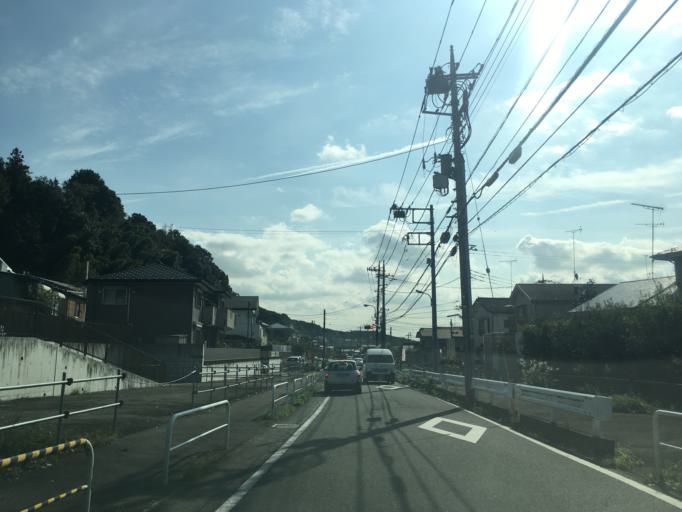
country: JP
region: Tokyo
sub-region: Machida-shi
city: Machida
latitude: 35.5952
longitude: 139.4121
